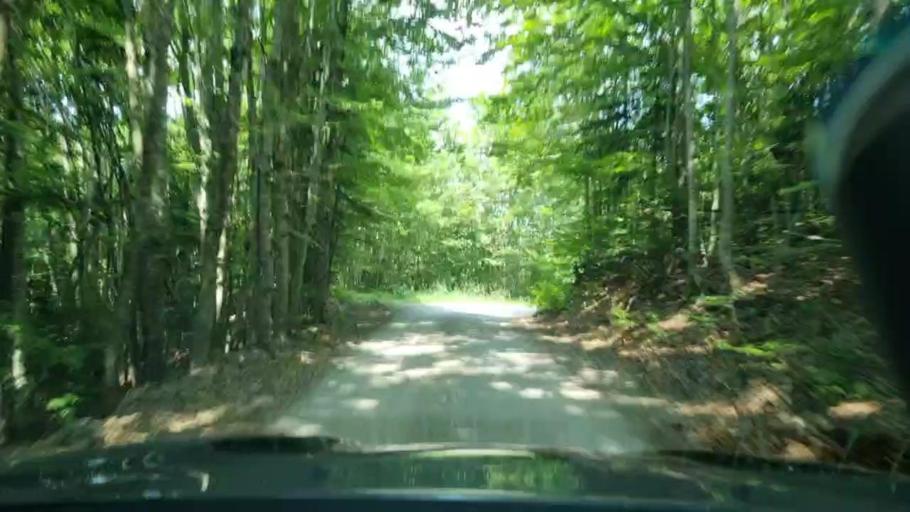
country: BA
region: Federation of Bosnia and Herzegovina
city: Bosansko Grahovo
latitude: 44.3256
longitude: 16.2363
